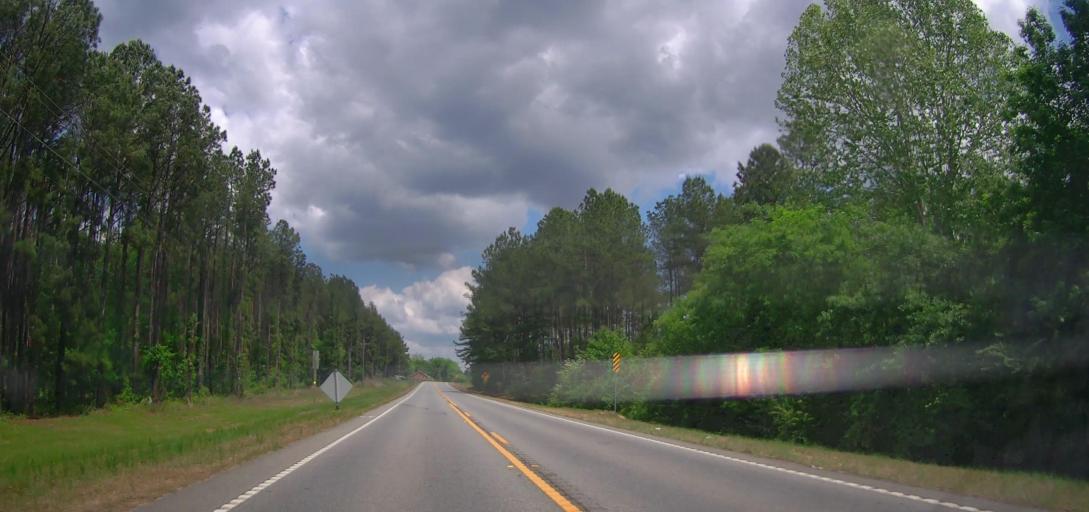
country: US
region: Georgia
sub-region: Laurens County
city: East Dublin
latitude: 32.5661
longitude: -82.8061
